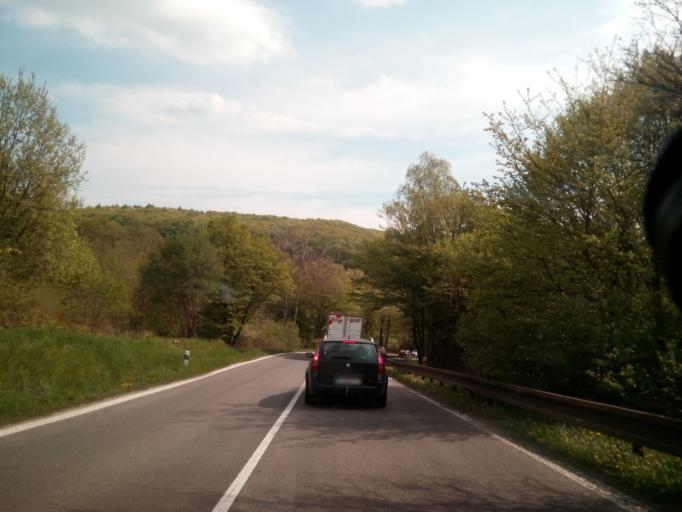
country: SK
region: Presovsky
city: Giraltovce
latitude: 49.0487
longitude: 21.4324
